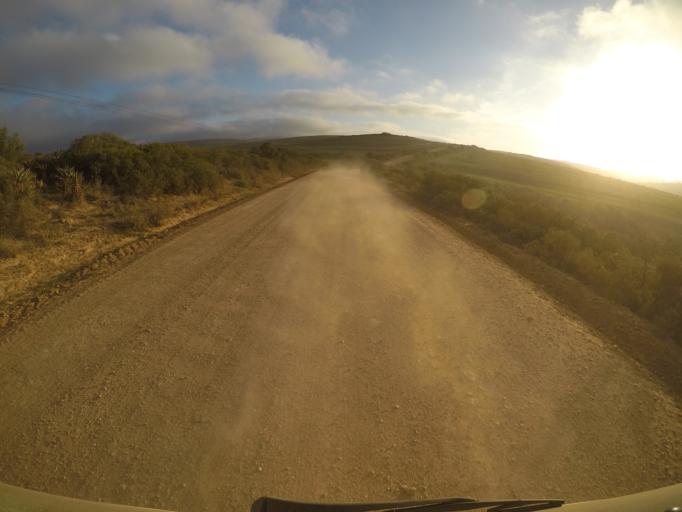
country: ZA
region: Western Cape
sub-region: Eden District Municipality
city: Mossel Bay
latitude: -34.1094
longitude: 22.0610
